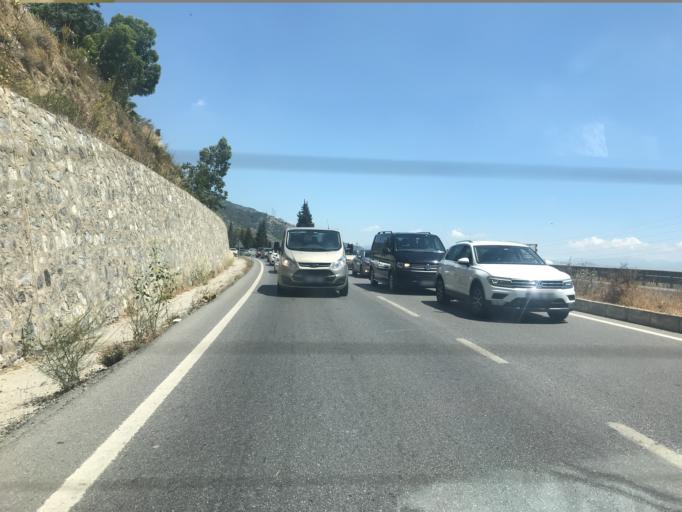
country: TR
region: Aydin
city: Soeke
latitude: 37.7875
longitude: 27.4659
